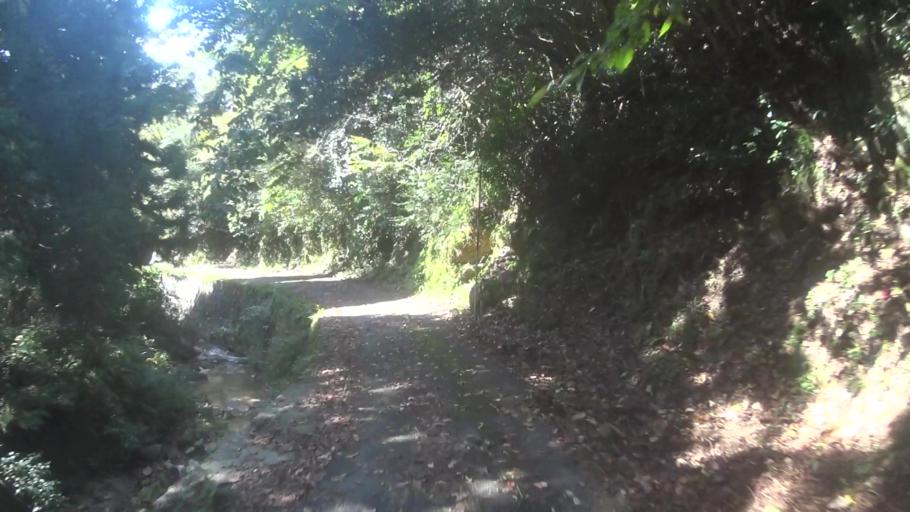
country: JP
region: Kyoto
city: Miyazu
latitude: 35.6996
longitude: 135.1294
